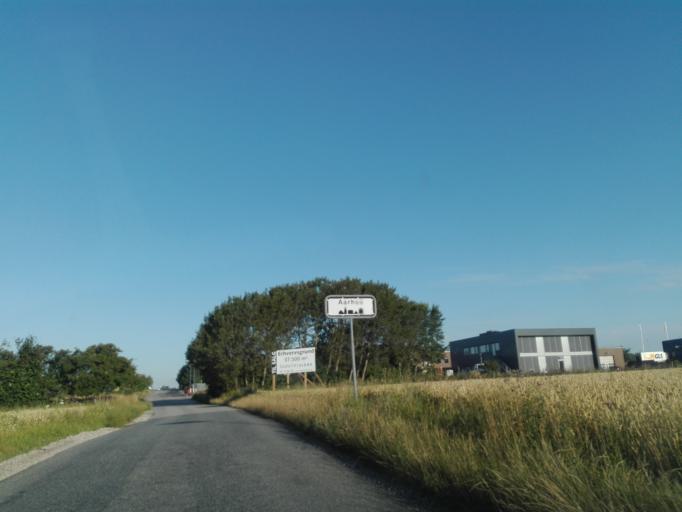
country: DK
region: Central Jutland
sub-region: Arhus Kommune
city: Tranbjerg
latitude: 56.1028
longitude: 10.1546
